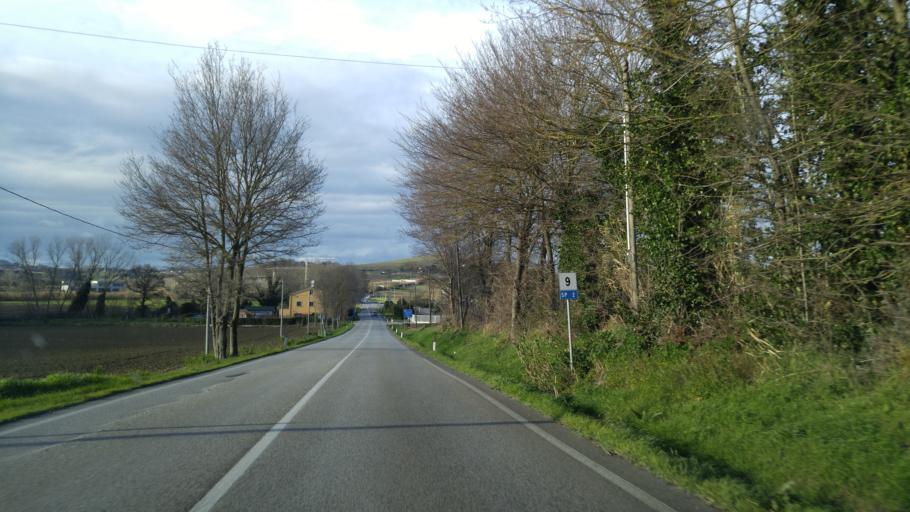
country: IT
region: The Marches
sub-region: Provincia di Ancona
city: Camerano
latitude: 43.5238
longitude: 13.5325
